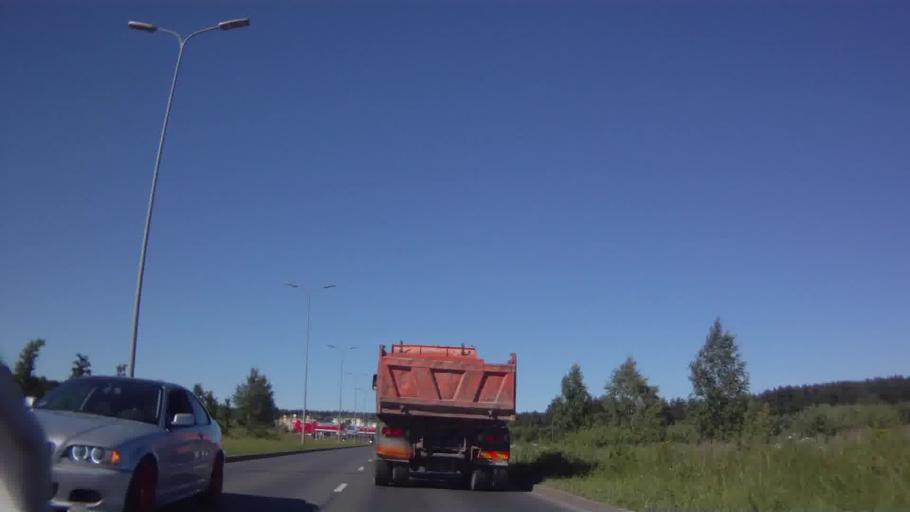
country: LV
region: Stopini
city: Ulbroka
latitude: 56.9531
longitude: 24.2512
